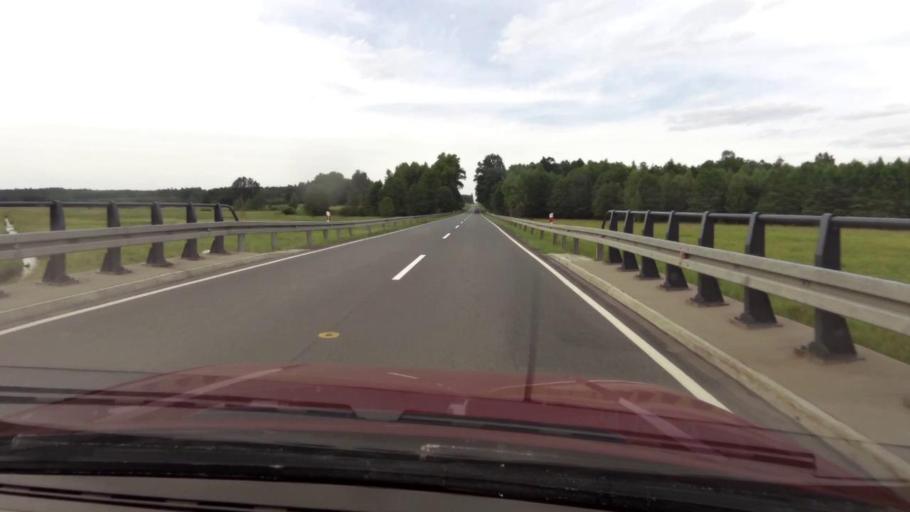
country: PL
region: Pomeranian Voivodeship
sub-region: Powiat bytowski
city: Trzebielino
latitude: 54.2337
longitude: 17.0892
